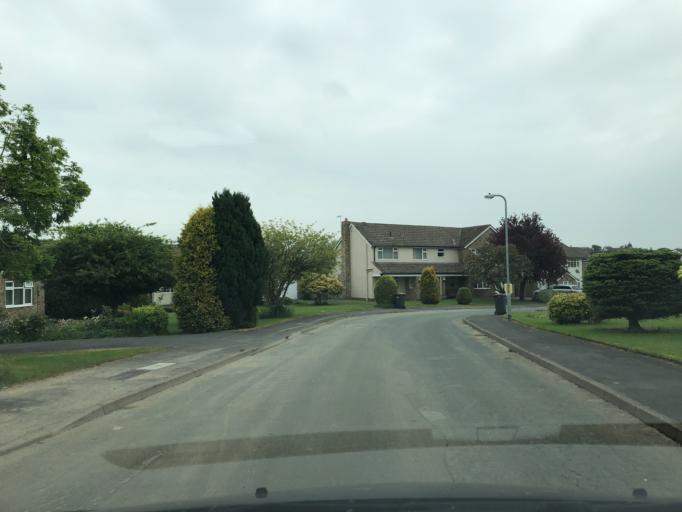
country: GB
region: England
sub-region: North Yorkshire
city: Harrogate
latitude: 54.0244
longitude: -1.5677
